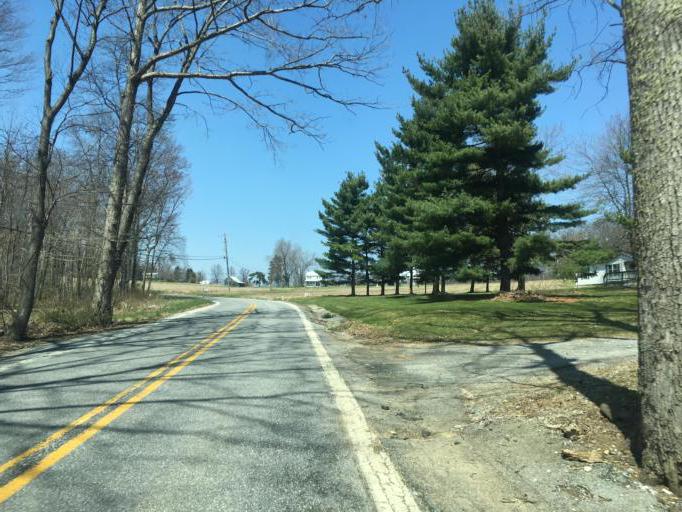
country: US
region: Maryland
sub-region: Washington County
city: Cavetown
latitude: 39.6195
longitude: -77.5571
